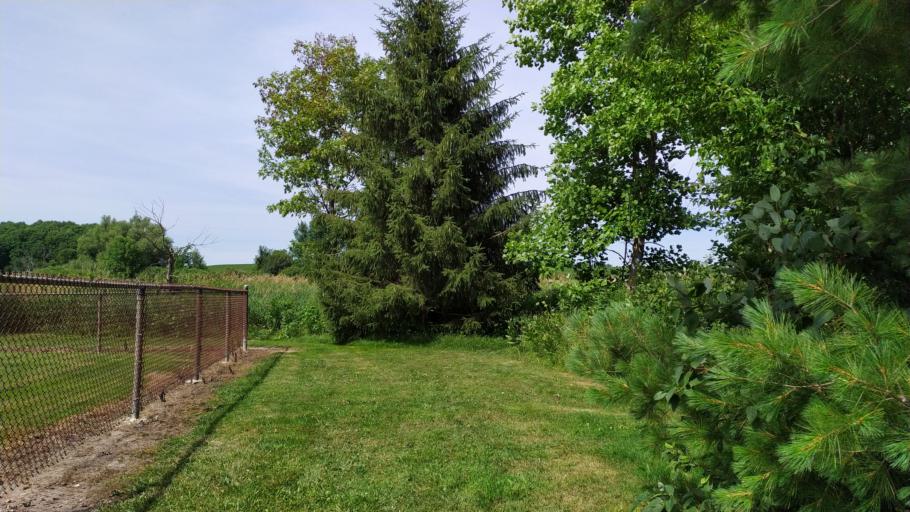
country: CA
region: Ontario
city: Stratford
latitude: 43.3757
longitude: -80.9438
